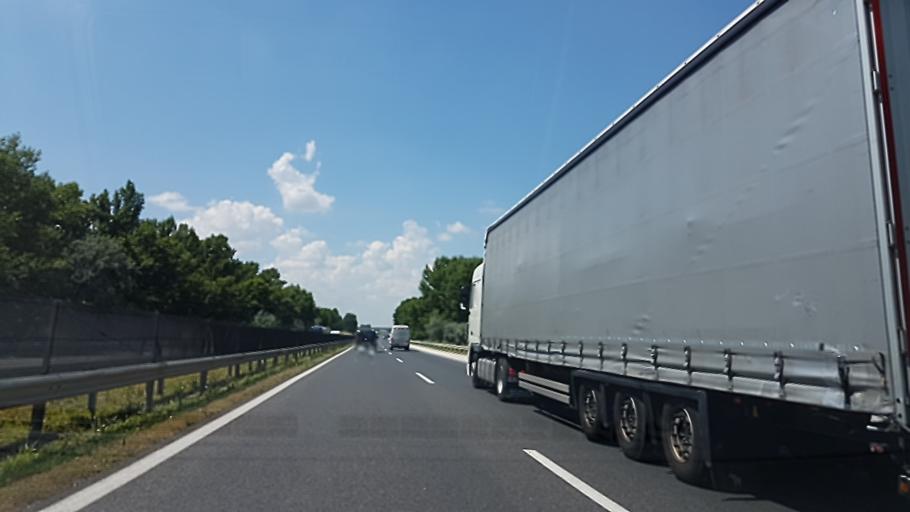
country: HU
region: Komarom-Esztergom
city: Kocs
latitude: 47.6290
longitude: 18.2600
